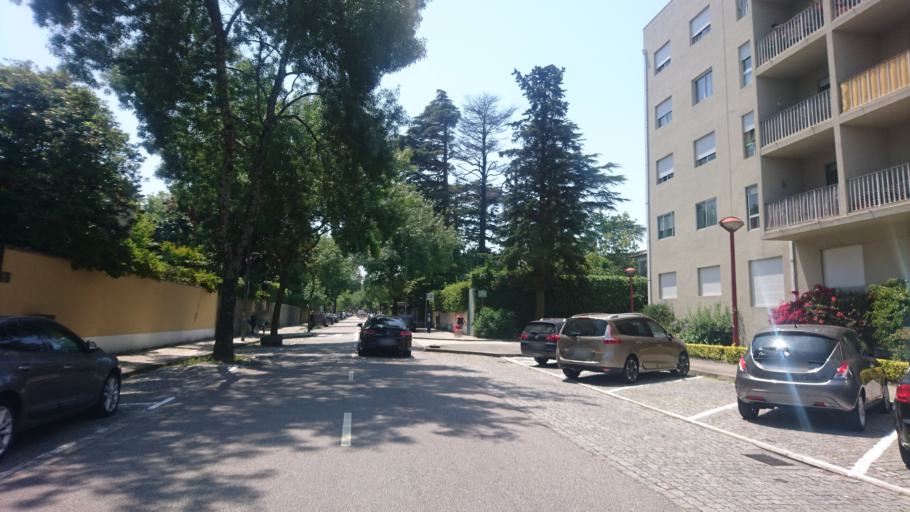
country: PT
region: Porto
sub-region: Porto
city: Porto
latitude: 41.1565
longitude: -8.6417
